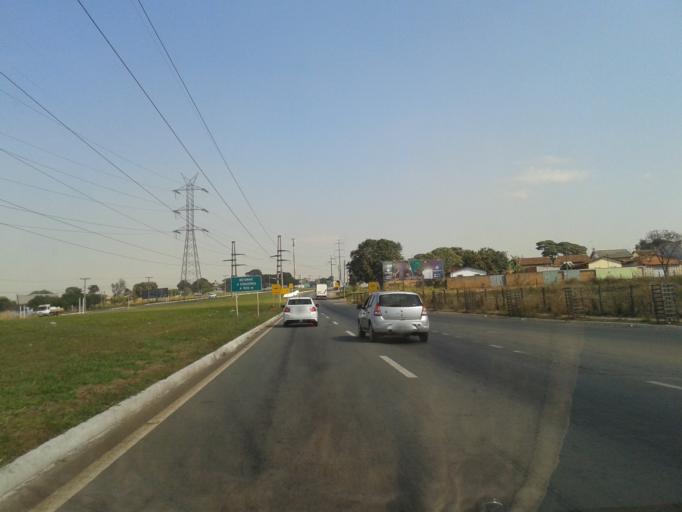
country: BR
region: Goias
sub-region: Aparecida De Goiania
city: Aparecida de Goiania
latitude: -16.7850
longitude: -49.2663
